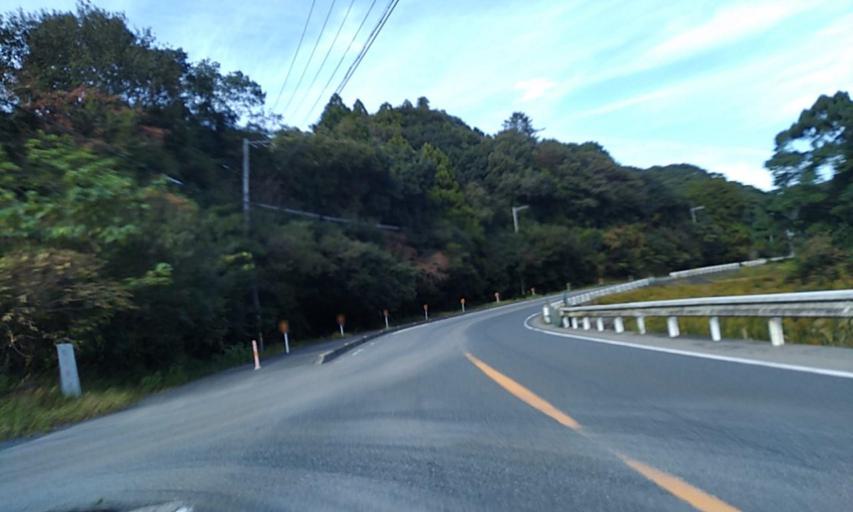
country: JP
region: Mie
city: Ise
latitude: 34.3547
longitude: 136.7417
